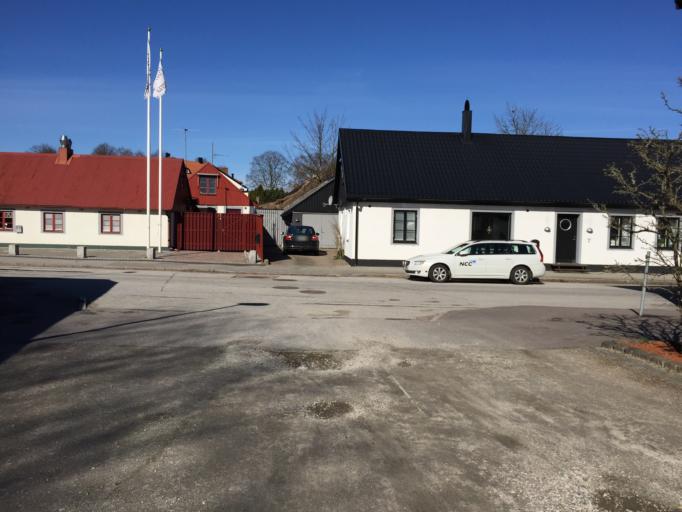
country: SE
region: Skane
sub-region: Lunds Kommun
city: Veberod
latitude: 55.6358
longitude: 13.4920
